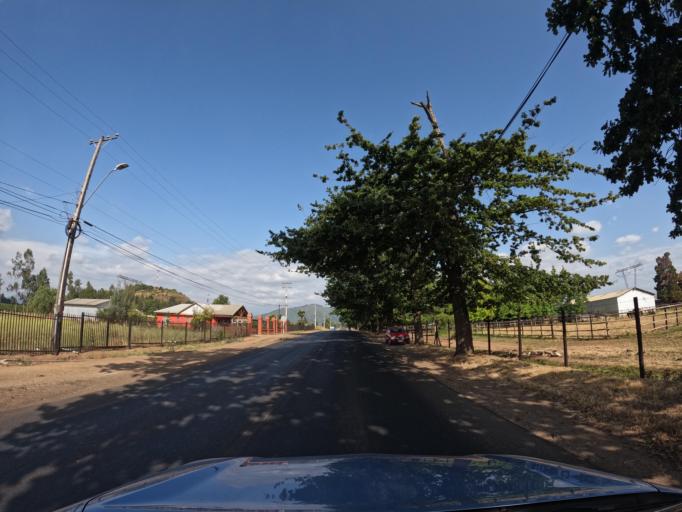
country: CL
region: Maule
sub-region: Provincia de Curico
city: Molina
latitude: -35.2797
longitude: -71.2696
